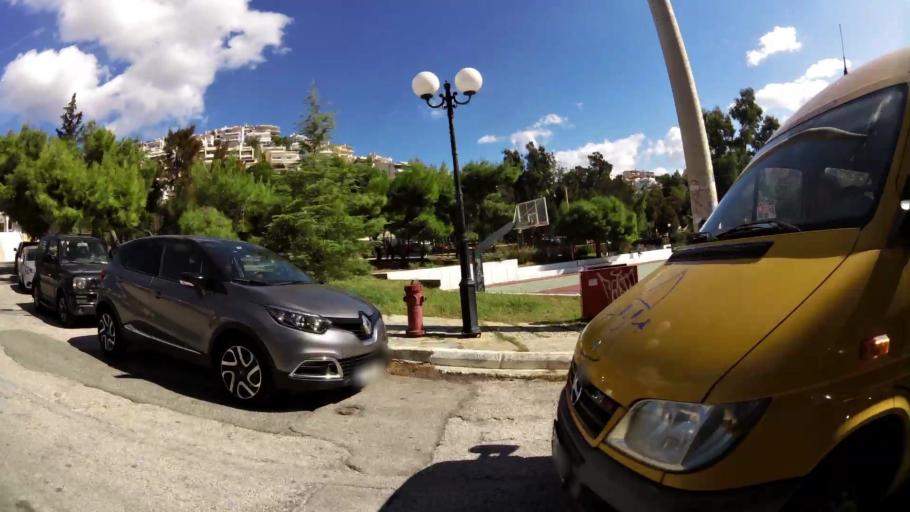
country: GR
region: Attica
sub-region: Nomarchia Anatolikis Attikis
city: Voula
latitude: 37.8541
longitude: 23.7784
